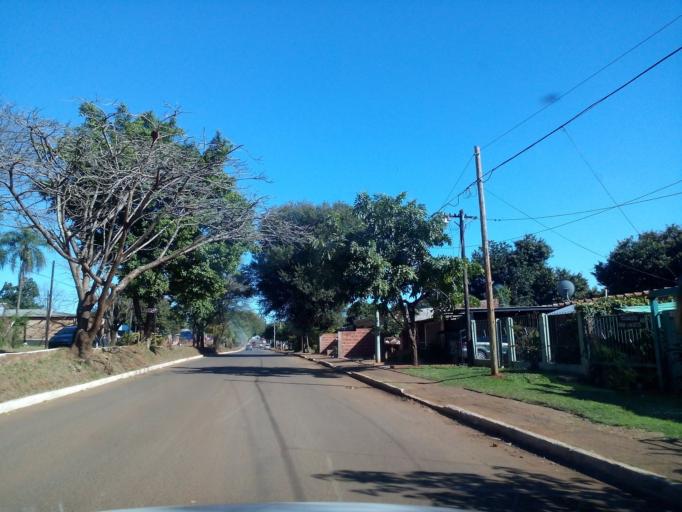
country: AR
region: Misiones
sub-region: Departamento de Capital
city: Posadas
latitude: -27.3769
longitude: -55.9373
